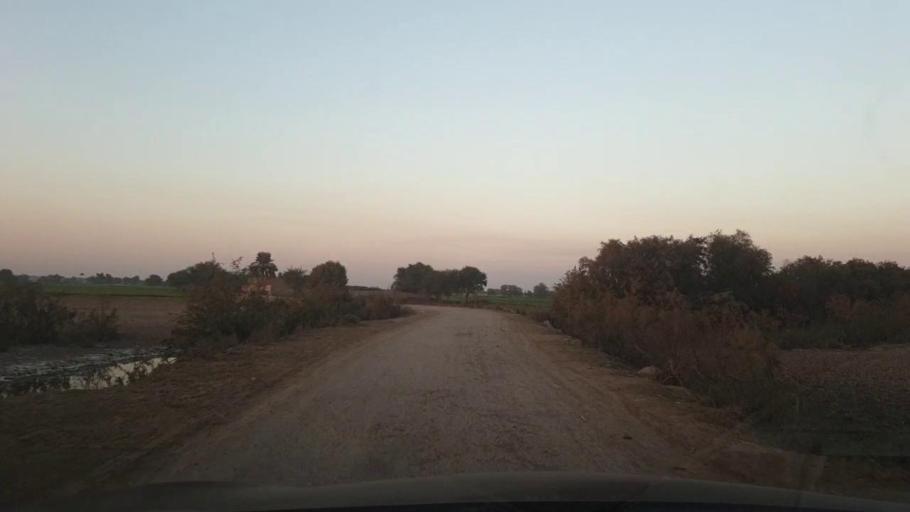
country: PK
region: Sindh
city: Ubauro
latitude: 28.1674
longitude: 69.6357
